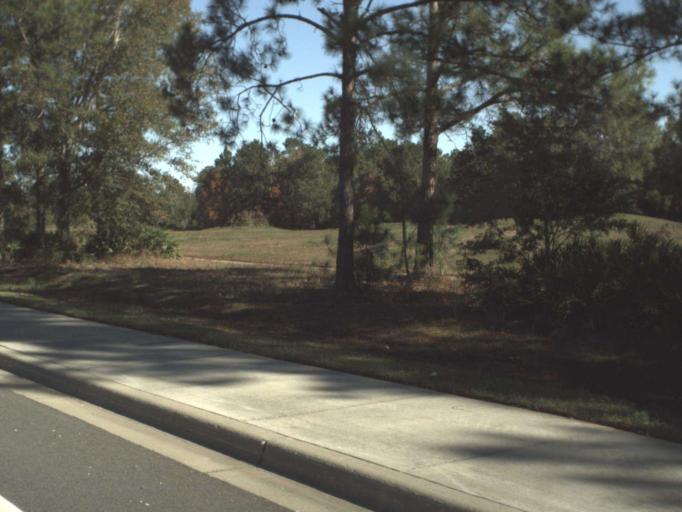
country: US
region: Florida
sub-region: Santa Rosa County
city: Bagdad
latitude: 30.5552
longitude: -87.0870
